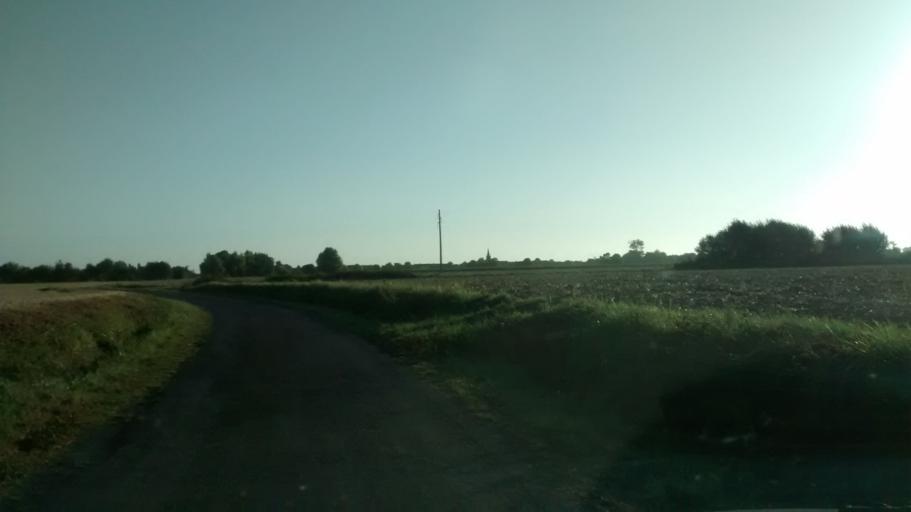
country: FR
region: Brittany
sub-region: Departement d'Ille-et-Vilaine
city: La Fresnais
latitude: 48.6069
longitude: -1.8526
